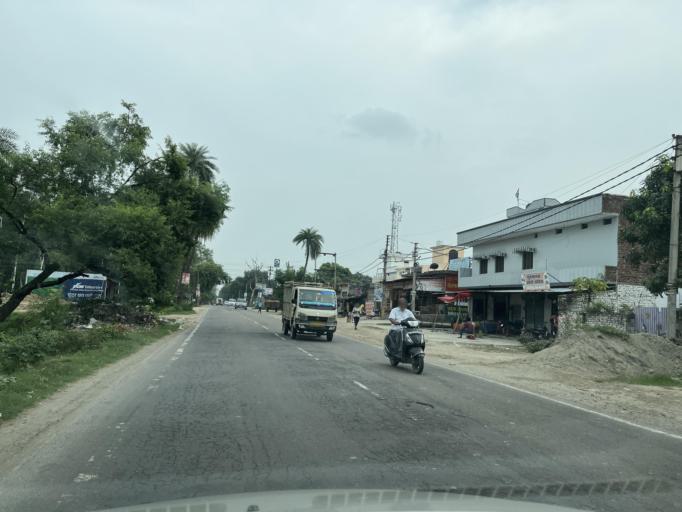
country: IN
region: Uttar Pradesh
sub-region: Rampur
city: Bilaspur
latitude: 29.0321
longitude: 79.2611
